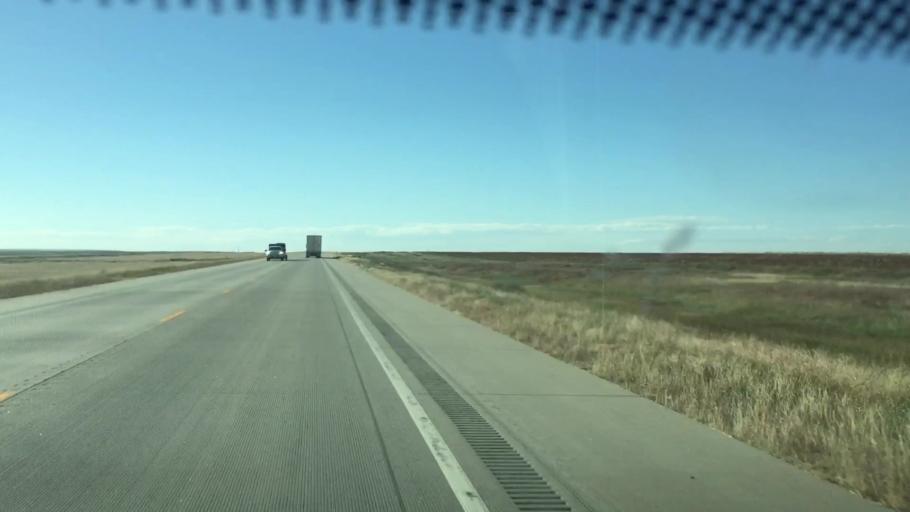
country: US
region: Colorado
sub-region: Kiowa County
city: Eads
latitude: 38.7876
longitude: -102.9255
